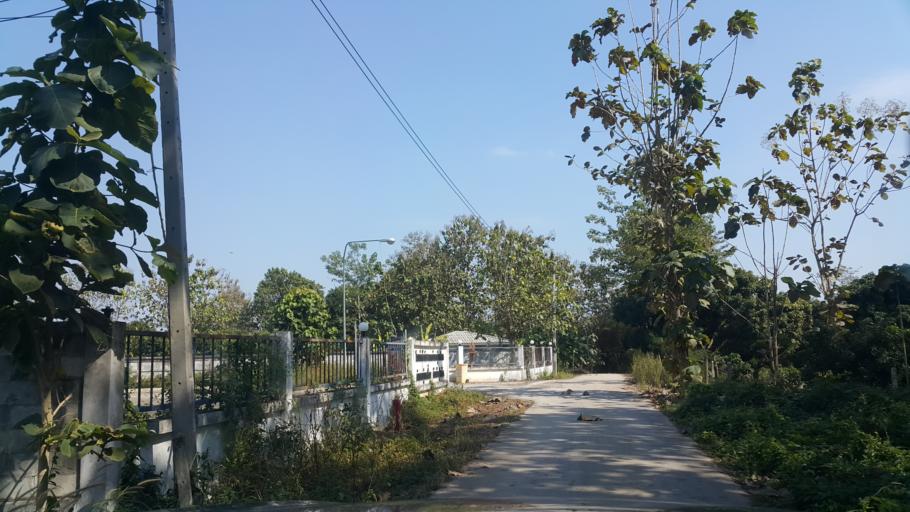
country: TH
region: Sukhothai
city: Thung Saliam
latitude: 17.3195
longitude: 99.5771
